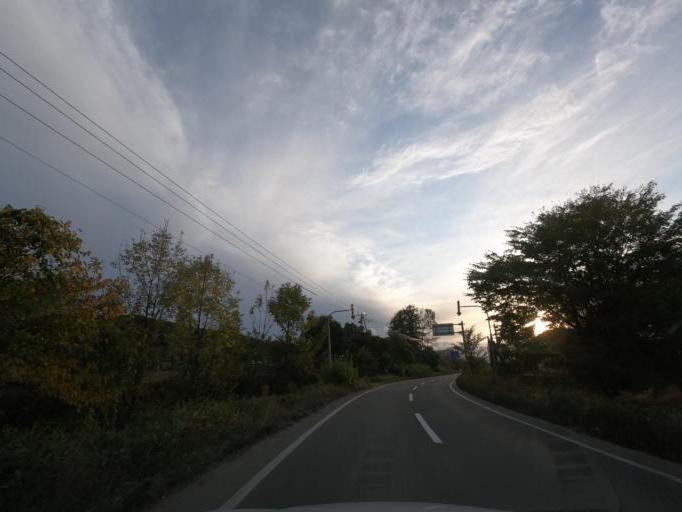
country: JP
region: Hokkaido
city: Obihiro
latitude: 42.5684
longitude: 143.3169
